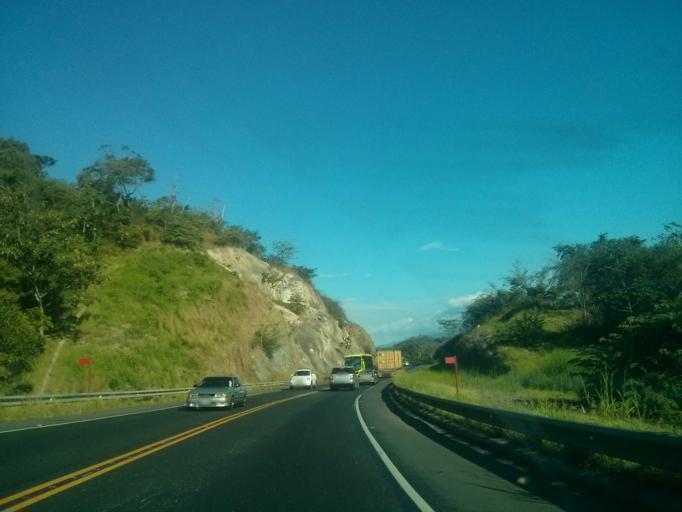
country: CR
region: Alajuela
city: Atenas
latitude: 9.9415
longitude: -84.3910
